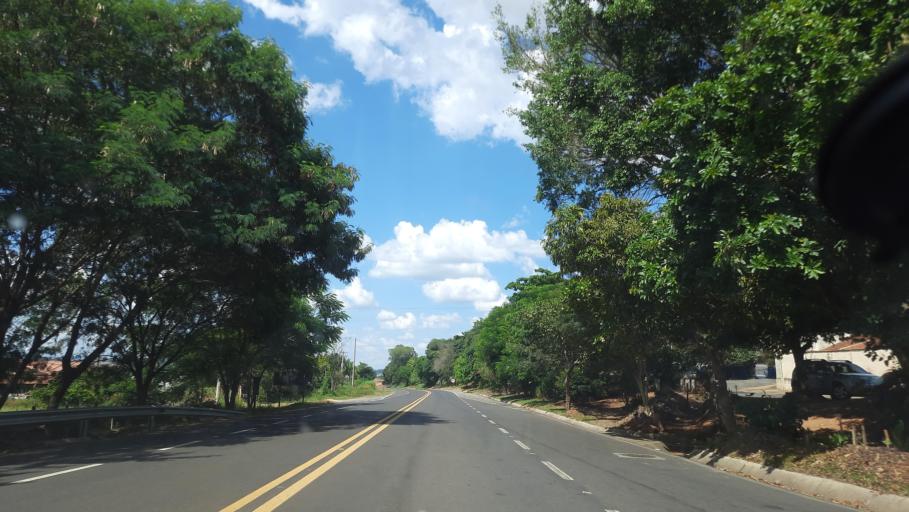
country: BR
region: Sao Paulo
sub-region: Sao Jose Do Rio Pardo
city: Sao Jose do Rio Pardo
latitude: -21.6061
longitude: -46.9319
